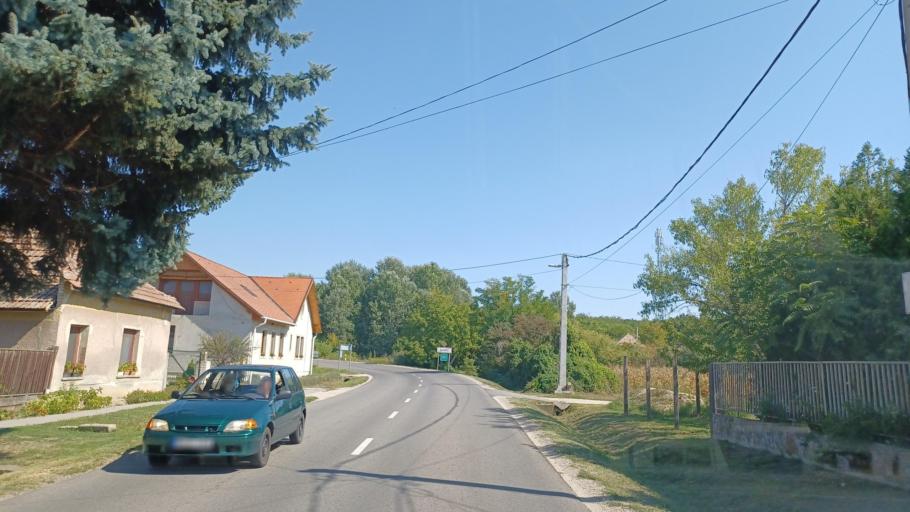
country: HU
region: Tolna
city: Nagydorog
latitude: 46.6798
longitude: 18.6672
